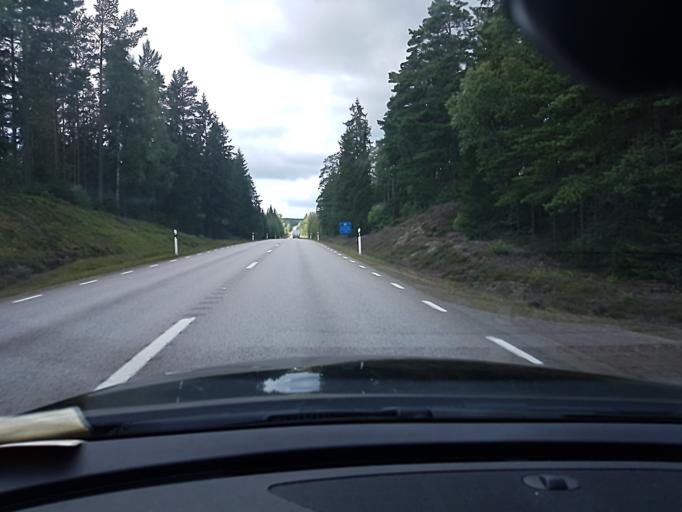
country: SE
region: Kronoberg
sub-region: Lessebo Kommun
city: Lessebo
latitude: 56.7308
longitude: 15.3852
